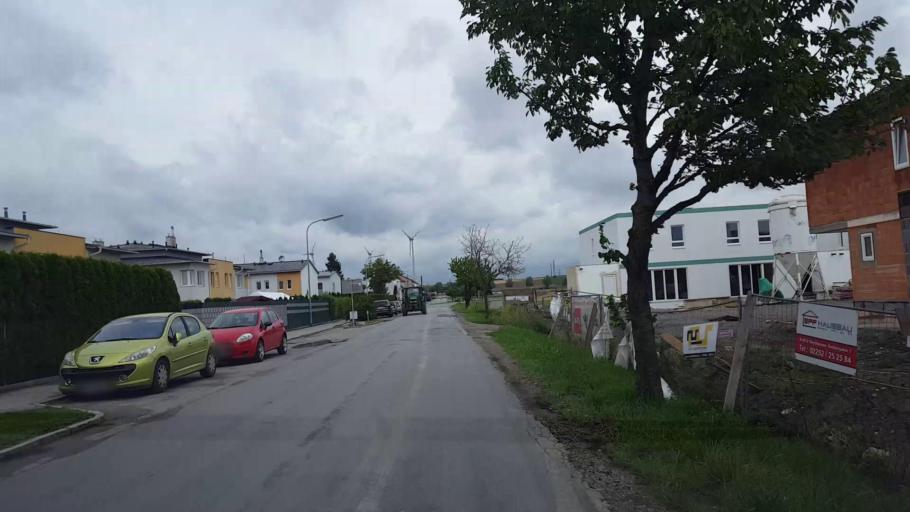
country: AT
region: Lower Austria
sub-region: Politischer Bezirk Bruck an der Leitha
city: Bruck an der Leitha
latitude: 48.0183
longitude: 16.7201
